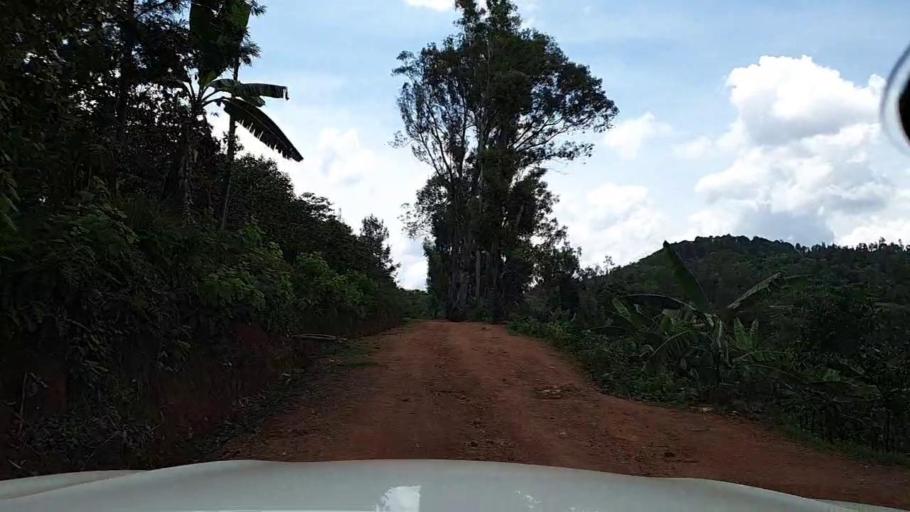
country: RW
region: Southern Province
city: Butare
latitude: -2.7521
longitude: 29.7580
